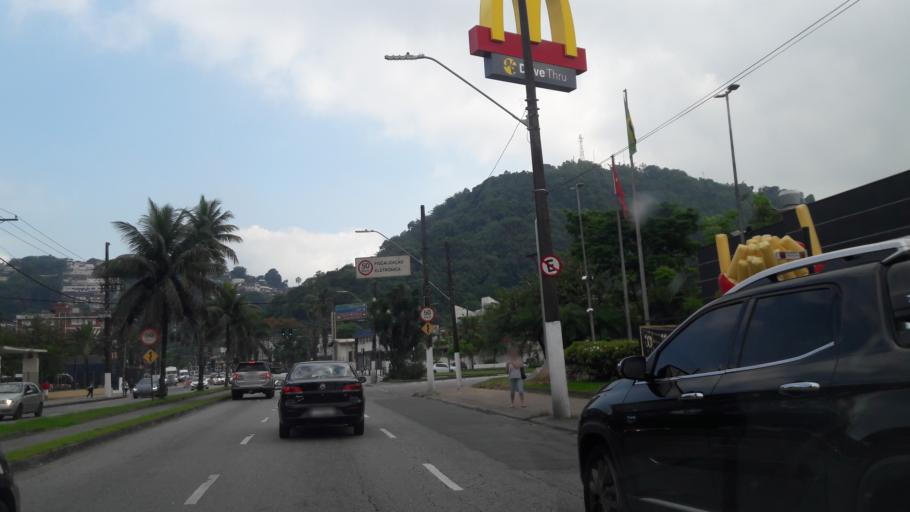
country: BR
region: Sao Paulo
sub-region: Santos
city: Santos
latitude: -23.9445
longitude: -46.3350
